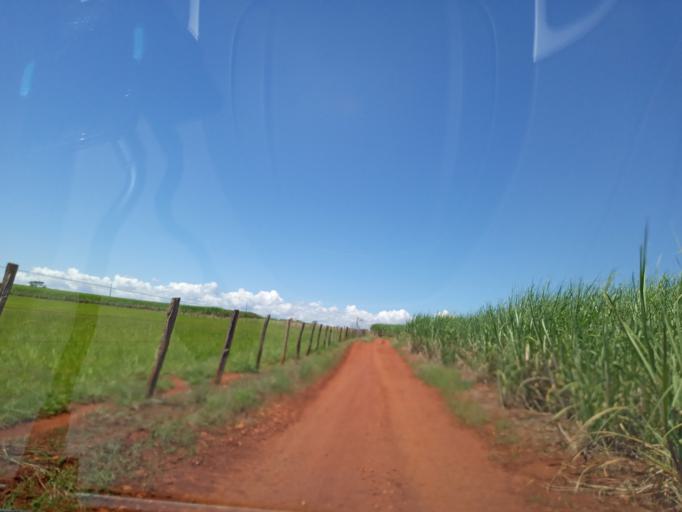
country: BR
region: Goias
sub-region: Itumbiara
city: Itumbiara
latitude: -18.4023
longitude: -49.1301
